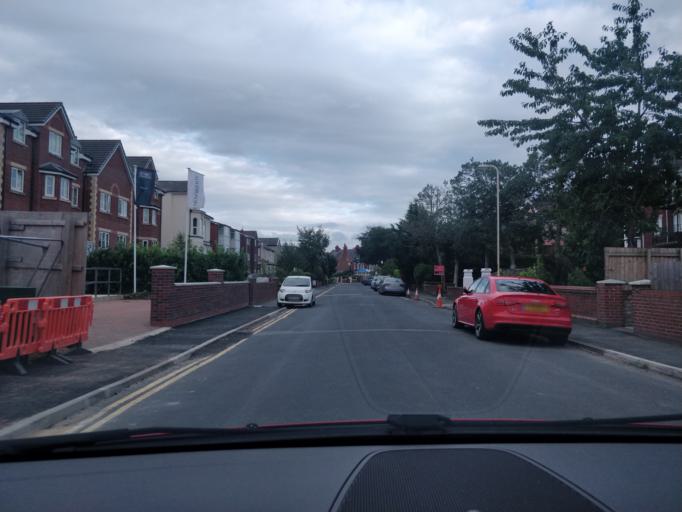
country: GB
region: England
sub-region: Sefton
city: Southport
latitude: 53.6516
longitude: -2.9909
